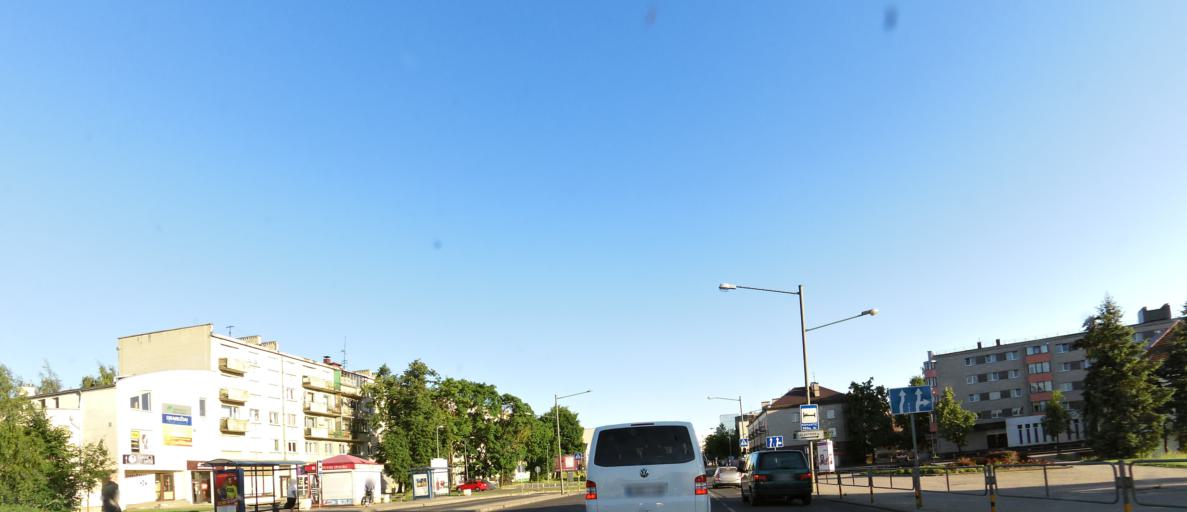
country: LT
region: Panevezys
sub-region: Panevezys City
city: Panevezys
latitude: 55.7298
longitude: 24.3673
